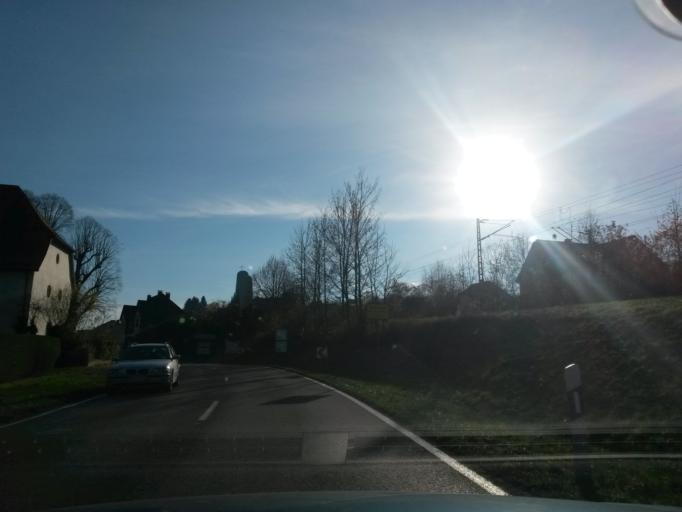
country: DE
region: Baden-Wuerttemberg
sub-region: Karlsruhe Region
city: Konigsbach-Stein
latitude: 48.9514
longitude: 8.6190
